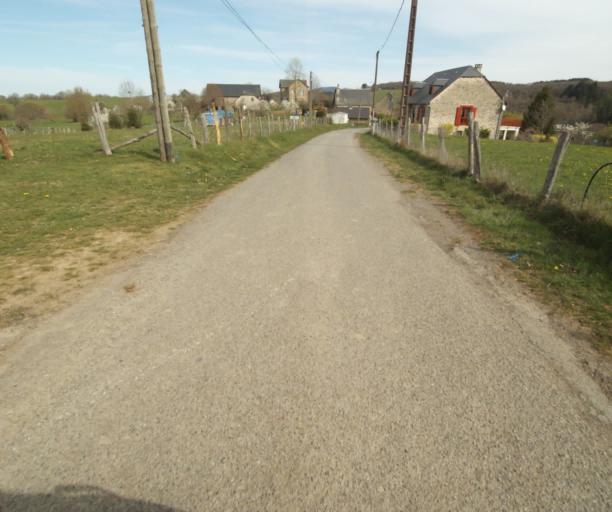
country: FR
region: Limousin
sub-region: Departement de la Correze
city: Correze
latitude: 45.3857
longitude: 1.8225
